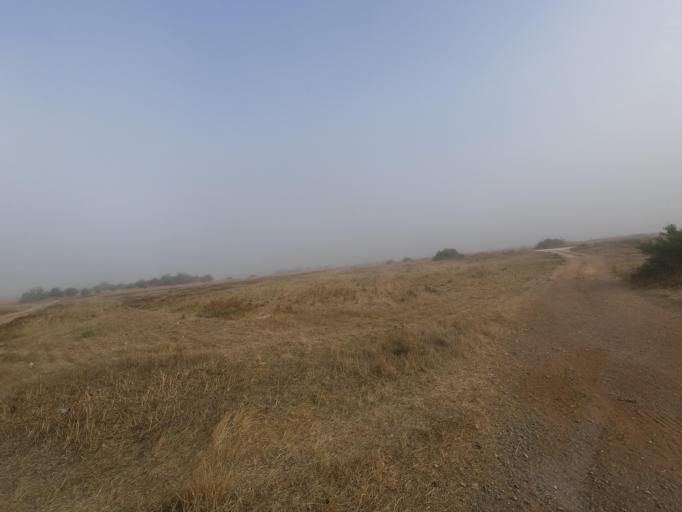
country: CY
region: Ammochostos
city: Acheritou
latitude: 35.0948
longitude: 33.8802
